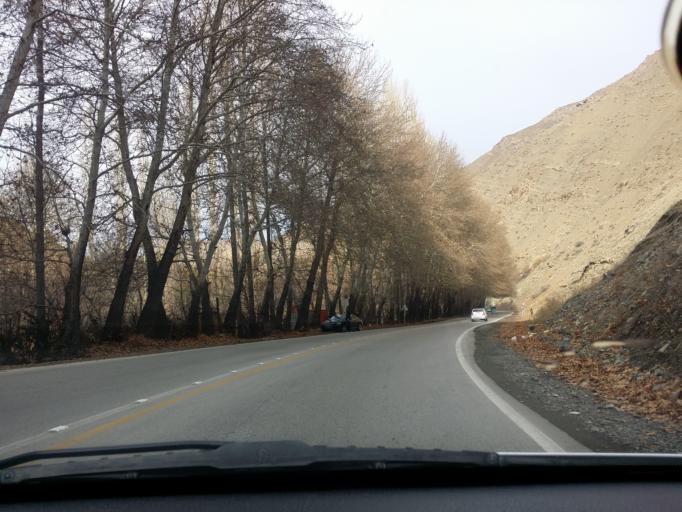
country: IR
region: Tehran
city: Tajrish
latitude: 36.0248
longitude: 51.2482
